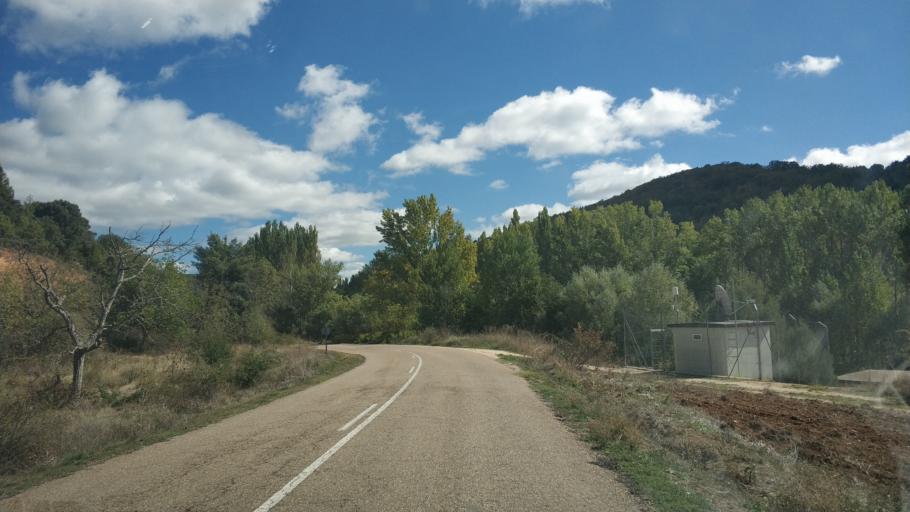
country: ES
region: Castille and Leon
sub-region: Provincia de Burgos
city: Covarrubias
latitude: 42.0544
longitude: -3.5089
